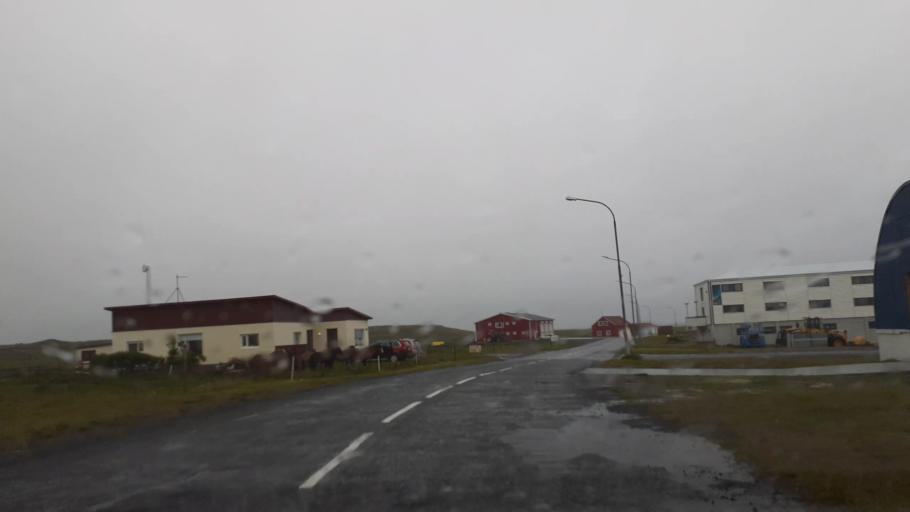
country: IS
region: Northeast
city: Husavik
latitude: 66.4575
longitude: -15.9504
